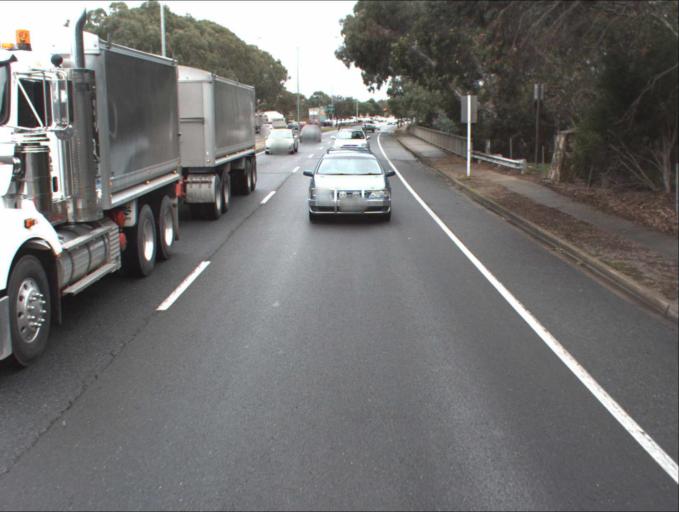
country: AU
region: South Australia
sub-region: Norwood Payneham St Peters
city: Marden
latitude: -34.8899
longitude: 138.6302
